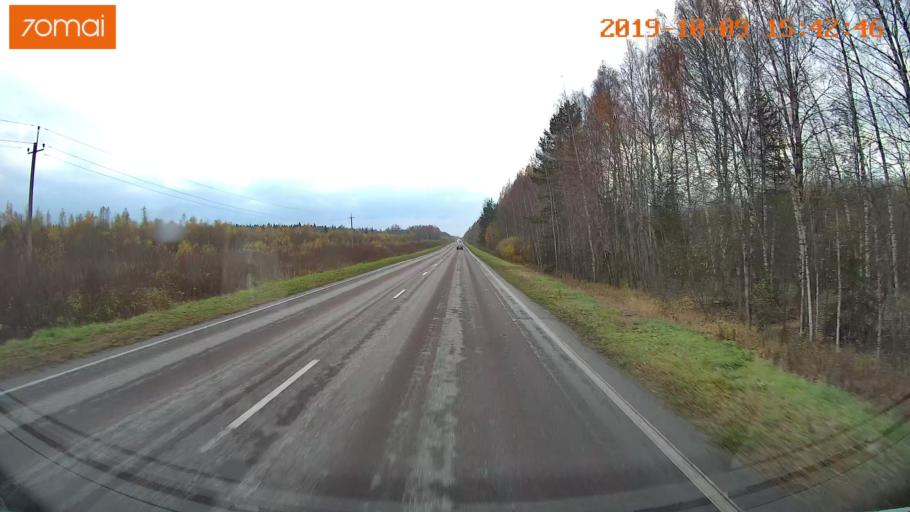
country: RU
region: Kostroma
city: Oktyabr'skiy
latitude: 57.8648
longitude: 41.1007
